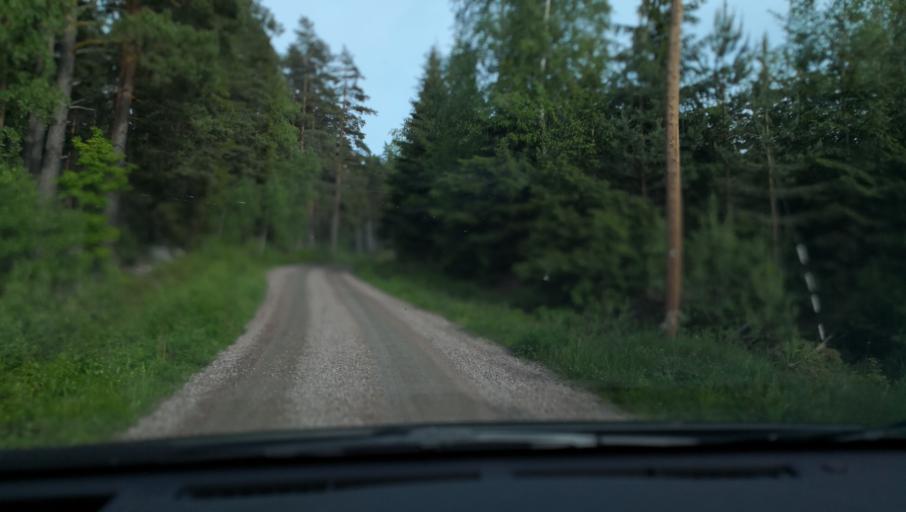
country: SE
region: Vaestmanland
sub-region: Arboga Kommun
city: Tyringe
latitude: 59.3646
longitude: 15.9984
